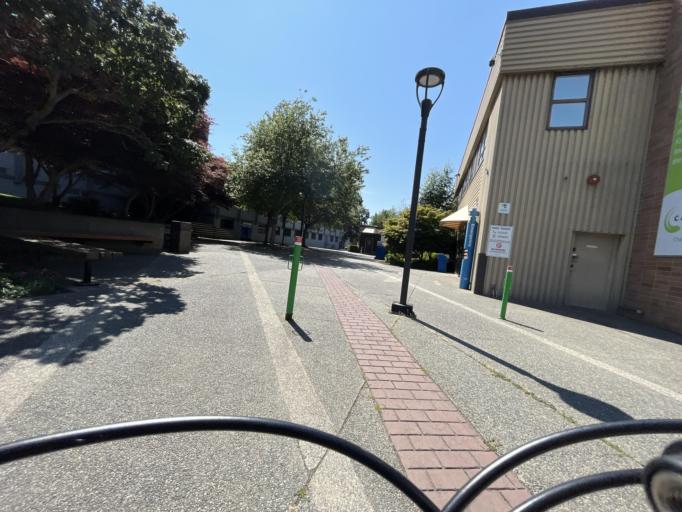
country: CA
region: British Columbia
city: Oak Bay
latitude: 48.4481
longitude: -123.3220
